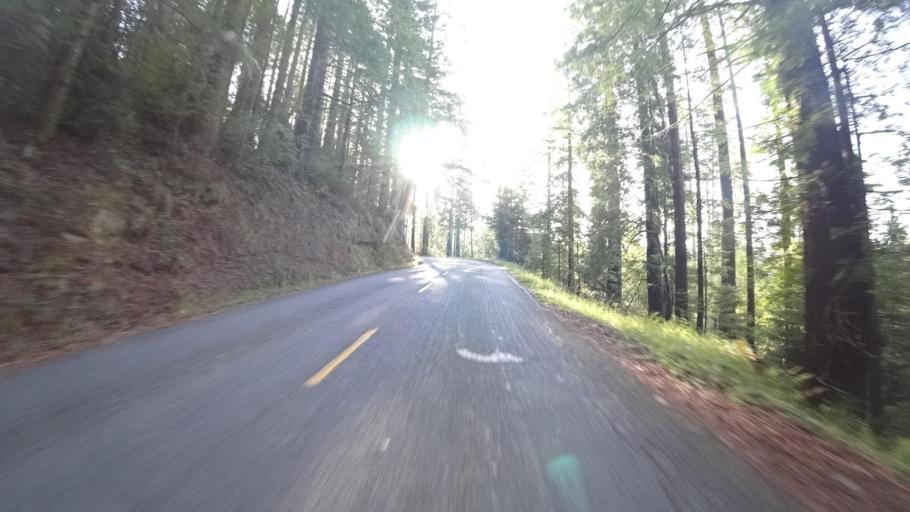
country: US
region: California
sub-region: Humboldt County
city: Bayside
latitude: 40.7568
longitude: -124.0325
